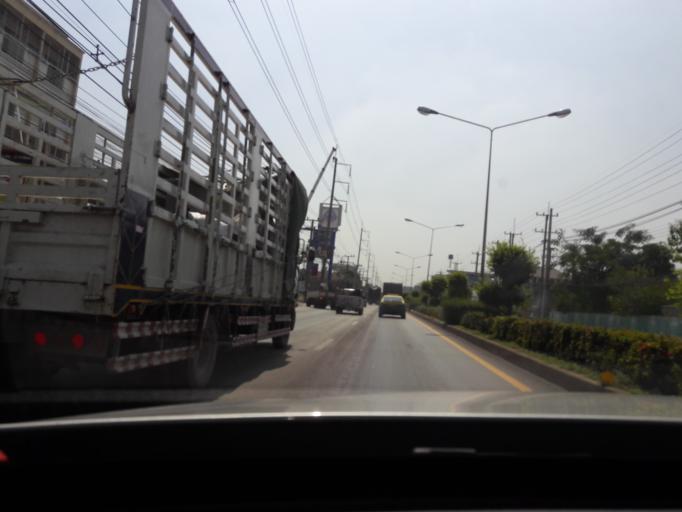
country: TH
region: Samut Sakhon
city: Samut Sakhon
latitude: 13.5890
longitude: 100.2801
